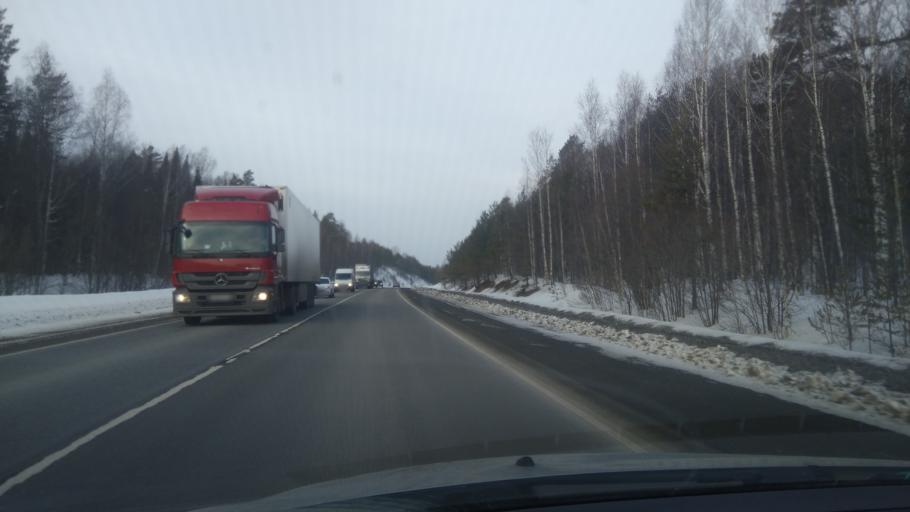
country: RU
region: Sverdlovsk
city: Bisert'
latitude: 56.8342
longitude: 58.8962
